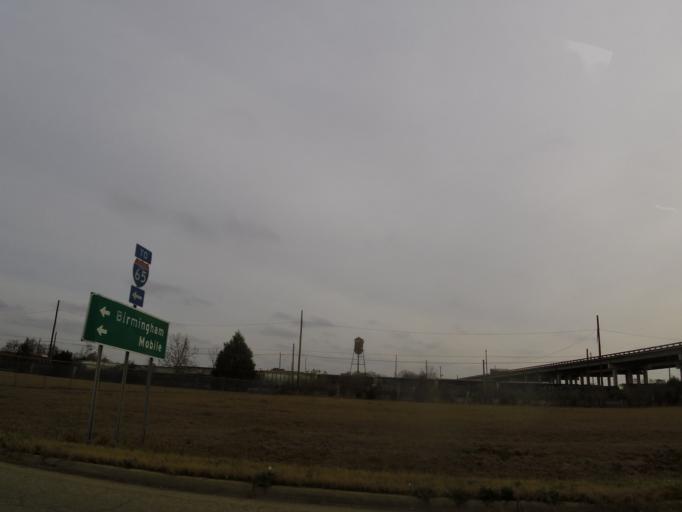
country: US
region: Alabama
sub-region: Montgomery County
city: Montgomery
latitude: 32.3963
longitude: -86.3169
